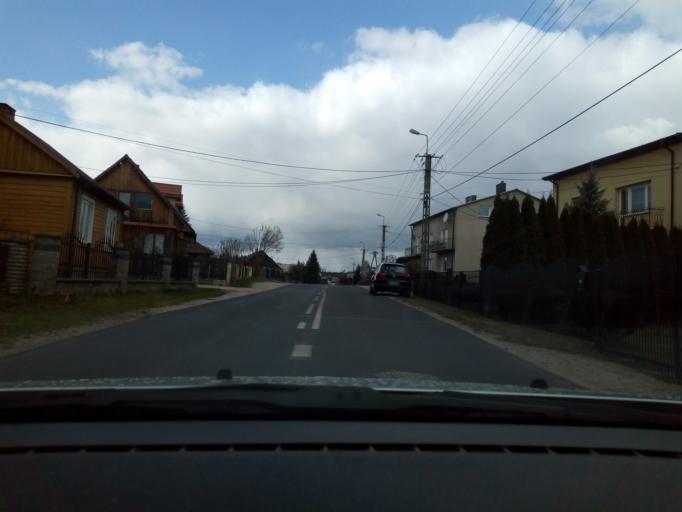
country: PL
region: Swietokrzyskie
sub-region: Powiat skarzyski
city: Skarzysko-Kamienna
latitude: 51.1521
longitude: 20.8626
